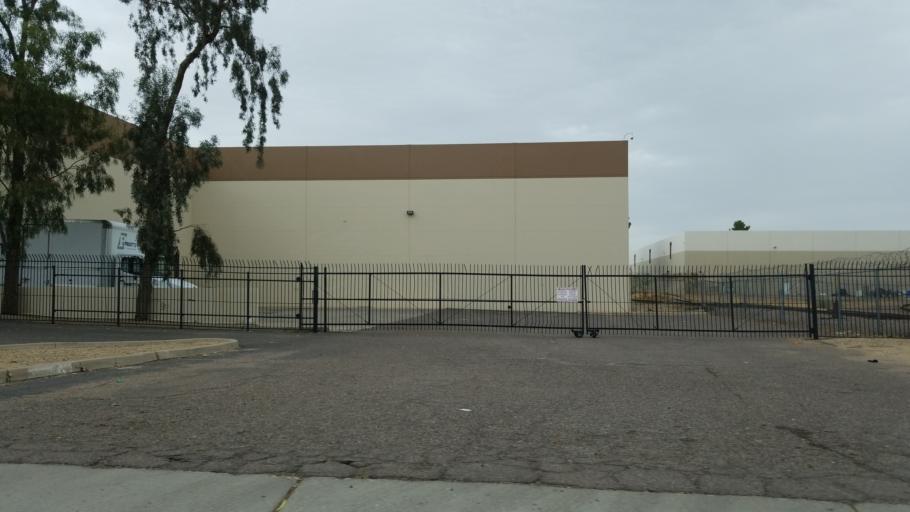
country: US
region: Arizona
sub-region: Maricopa County
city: Phoenix
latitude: 33.4477
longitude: -112.1496
